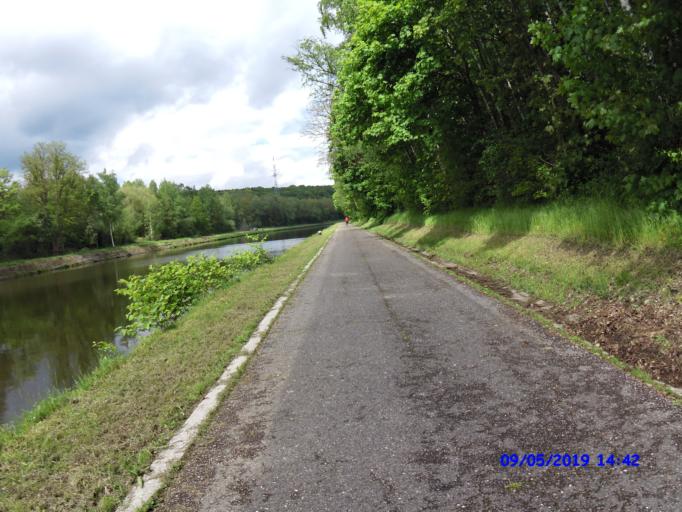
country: BE
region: Wallonia
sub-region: Province du Hainaut
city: Aiseau
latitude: 50.4501
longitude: 4.6109
